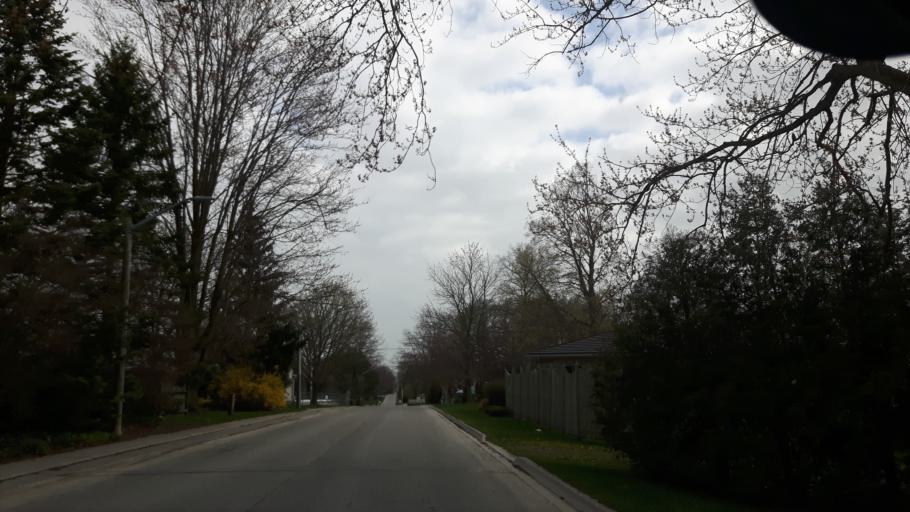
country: CA
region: Ontario
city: Bluewater
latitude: 43.6214
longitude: -81.5452
